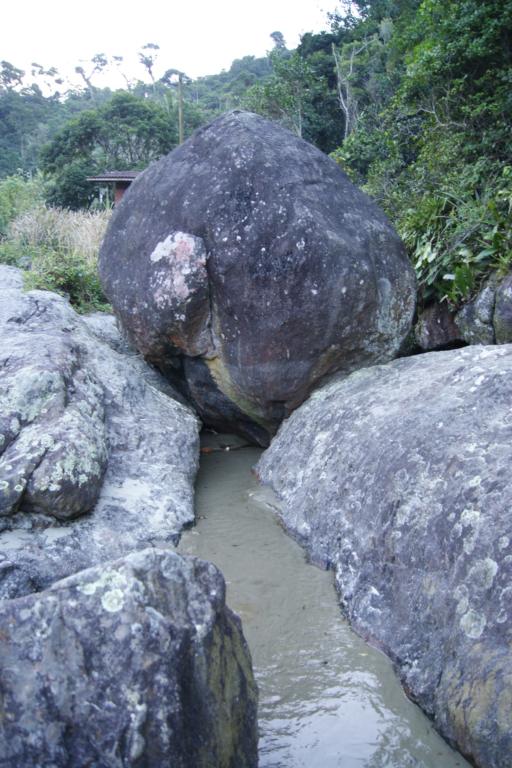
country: BR
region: Sao Paulo
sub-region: Peruibe
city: Peruibe
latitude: -24.3672
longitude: -47.0112
